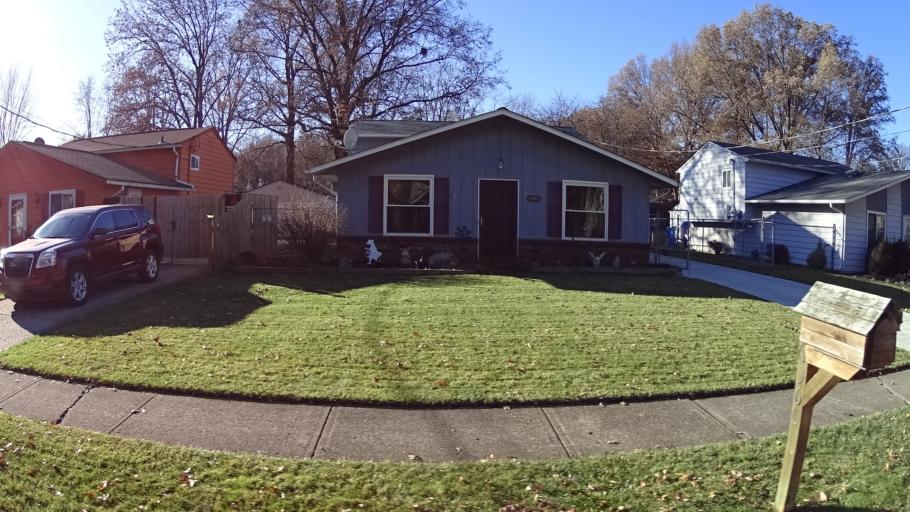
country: US
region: Ohio
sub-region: Lorain County
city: North Ridgeville
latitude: 41.3973
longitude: -82.0131
